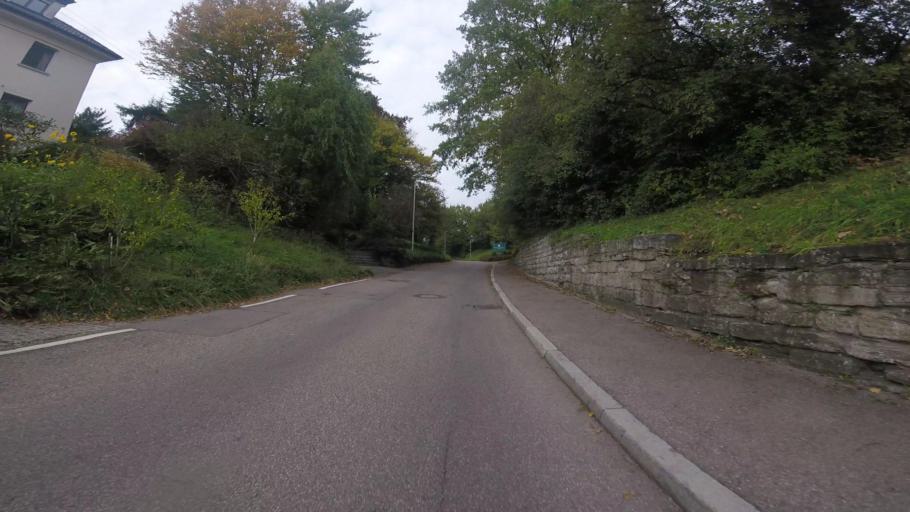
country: DE
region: Baden-Wuerttemberg
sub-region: Regierungsbezirk Stuttgart
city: Backnang
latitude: 48.9501
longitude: 9.4263
